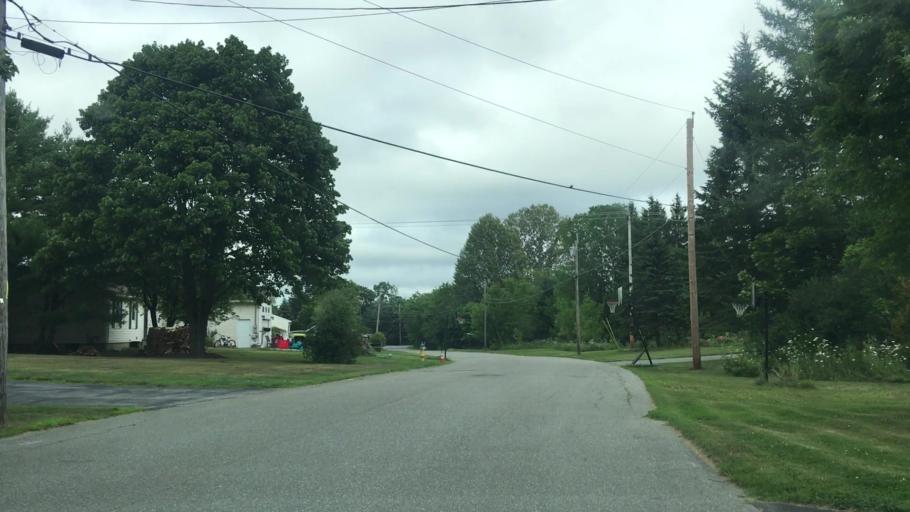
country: US
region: Maine
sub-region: Penobscot County
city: Brewer
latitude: 44.7722
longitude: -68.7702
